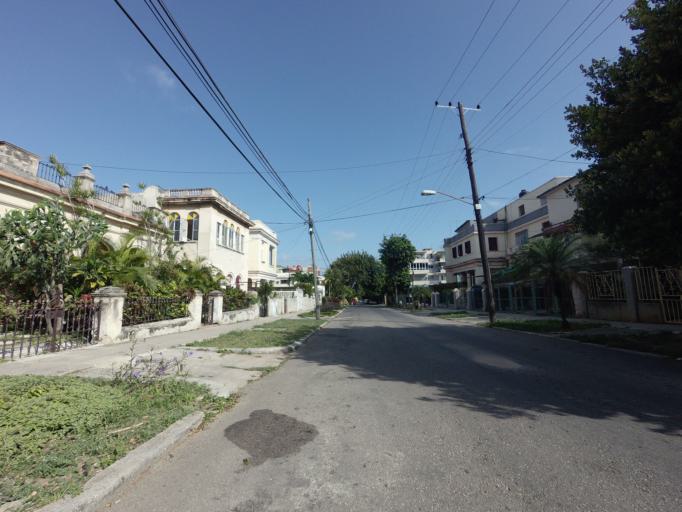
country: CU
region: La Habana
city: Havana
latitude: 23.1314
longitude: -82.3913
